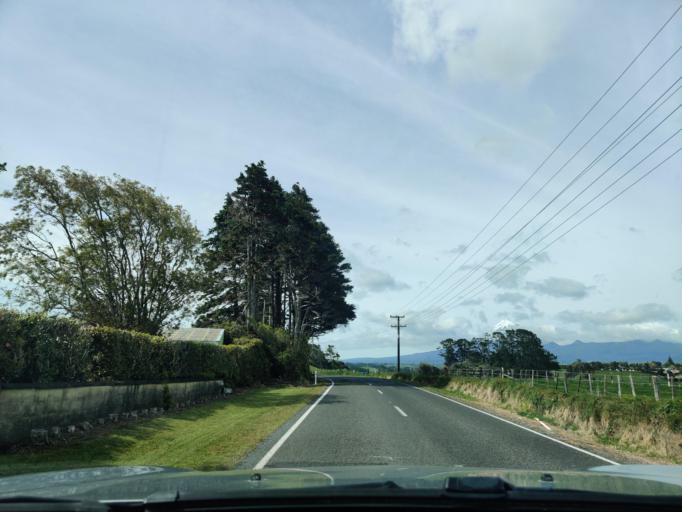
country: NZ
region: Taranaki
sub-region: New Plymouth District
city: New Plymouth
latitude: -39.1076
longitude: 174.1000
